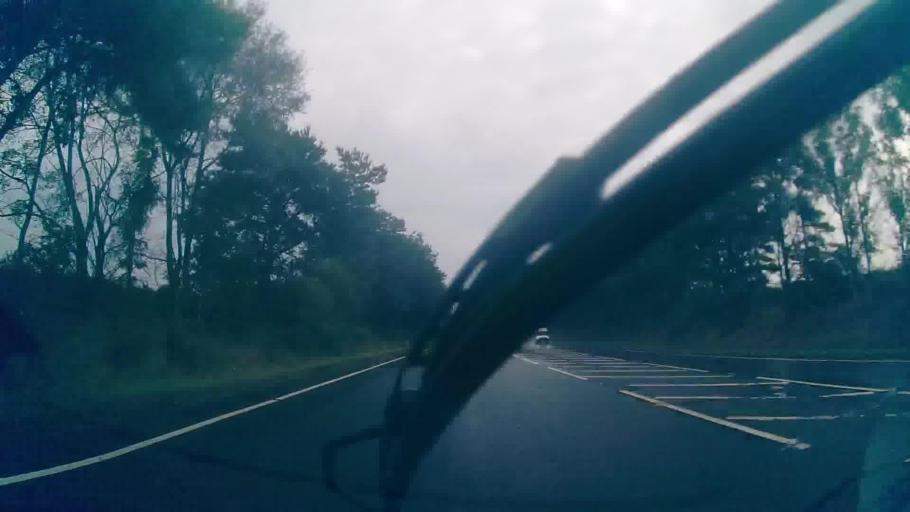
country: GB
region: Scotland
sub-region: Dumfries and Galloway
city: Locharbriggs
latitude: 55.0685
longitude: -3.5358
